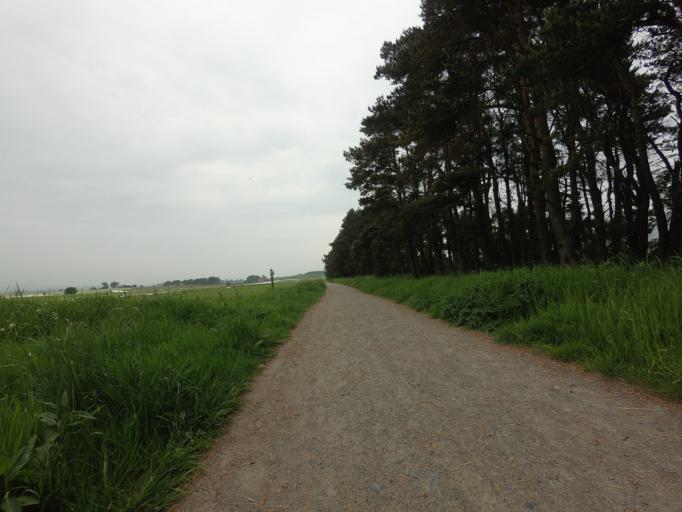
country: GB
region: Scotland
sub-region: Perth and Kinross
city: Milnathort
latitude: 56.2161
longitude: -3.3605
